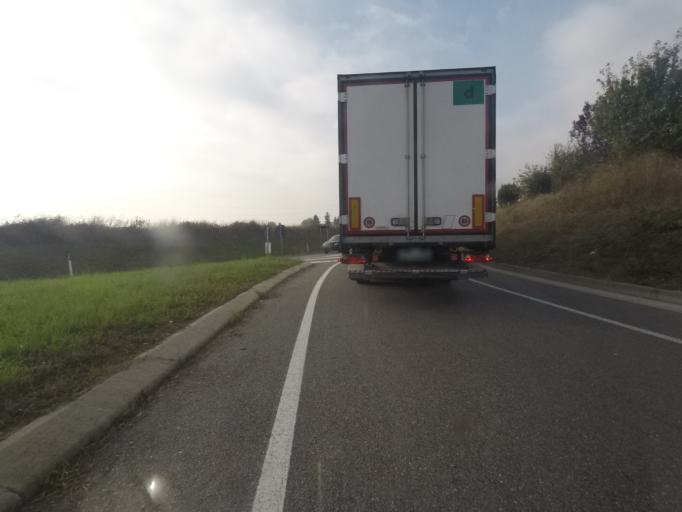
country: IT
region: Lombardy
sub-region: Provincia di Monza e Brianza
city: Burago di Molgora
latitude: 45.6085
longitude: 9.3829
